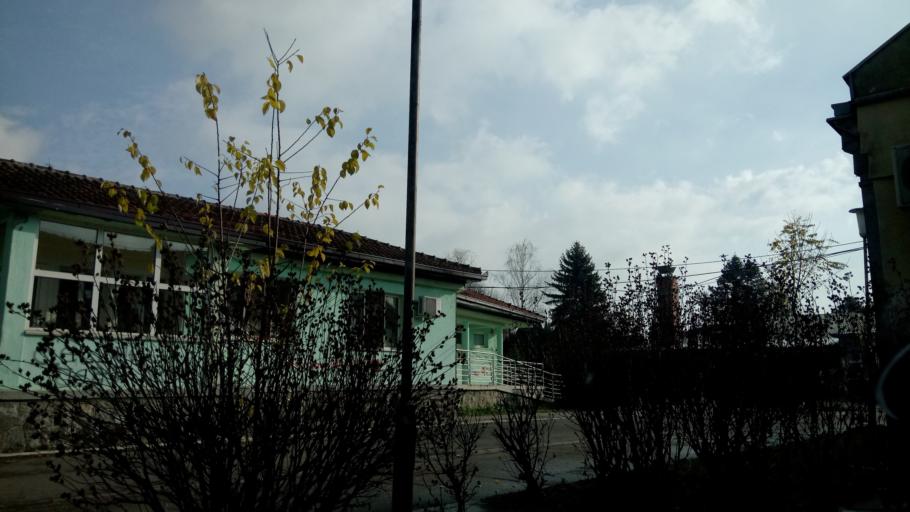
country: RS
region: Autonomna Pokrajina Vojvodina
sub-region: Sremski Okrug
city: Stara Pazova
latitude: 44.9825
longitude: 20.1569
